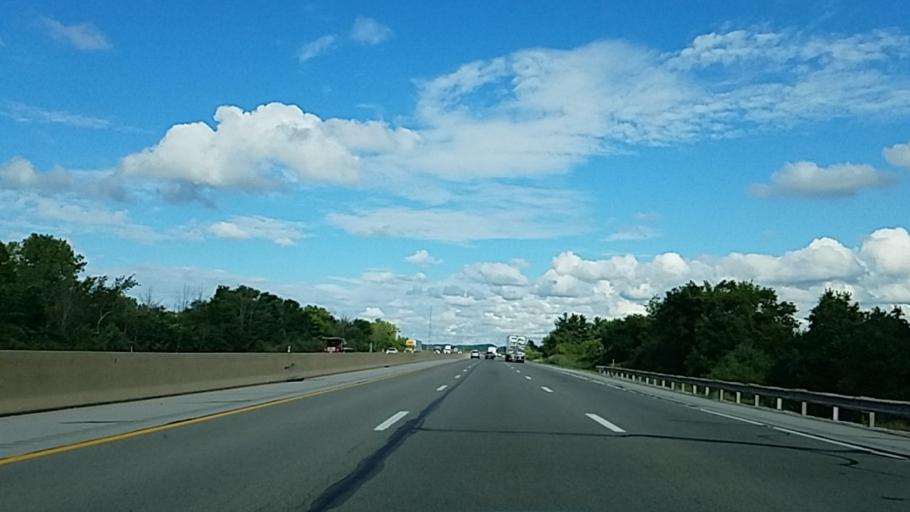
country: US
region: Ohio
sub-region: Erie County
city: Milan
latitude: 41.3244
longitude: -82.5588
